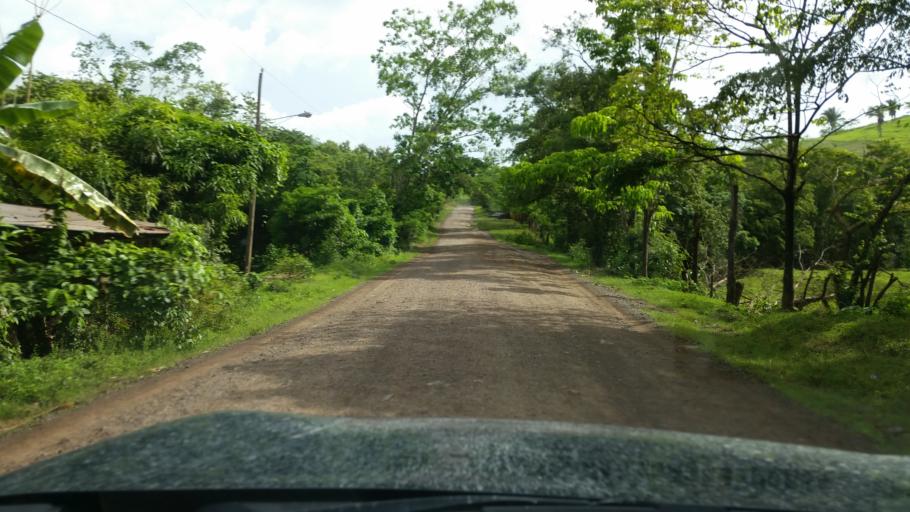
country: NI
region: Atlantico Norte (RAAN)
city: Siuna
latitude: 13.6013
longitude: -84.7998
